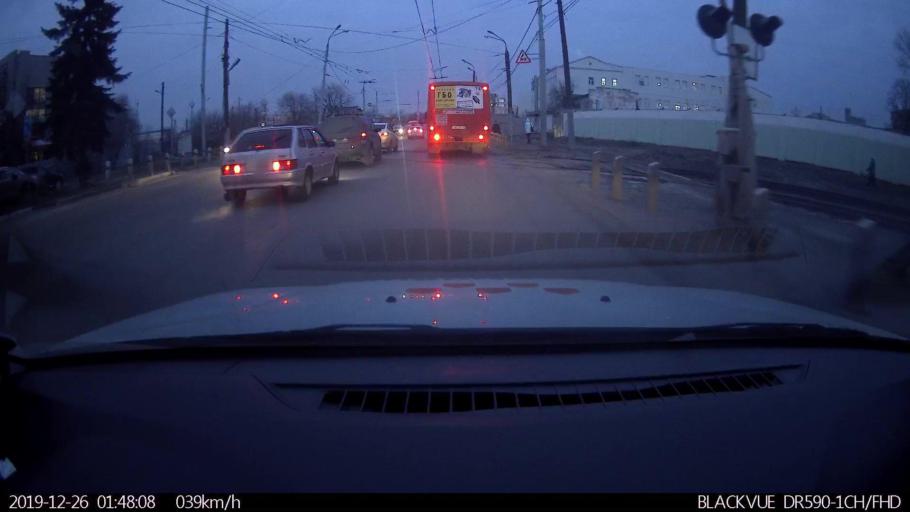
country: RU
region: Nizjnij Novgorod
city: Nizhniy Novgorod
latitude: 56.3117
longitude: 43.9455
